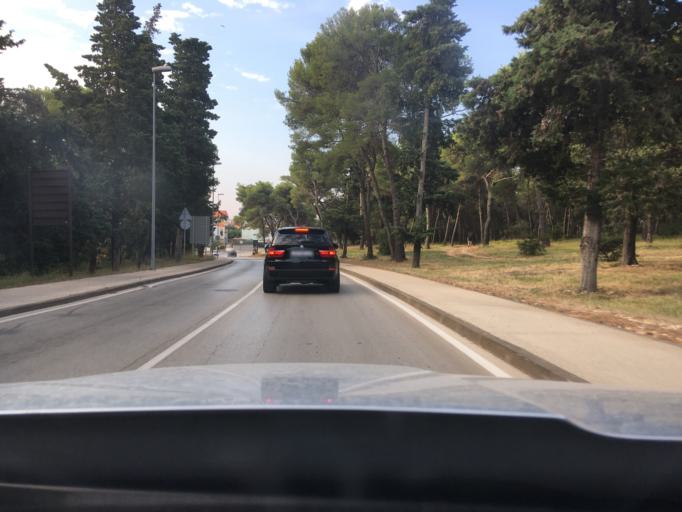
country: HR
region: Zadarska
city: Zadar
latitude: 44.1383
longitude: 15.2286
